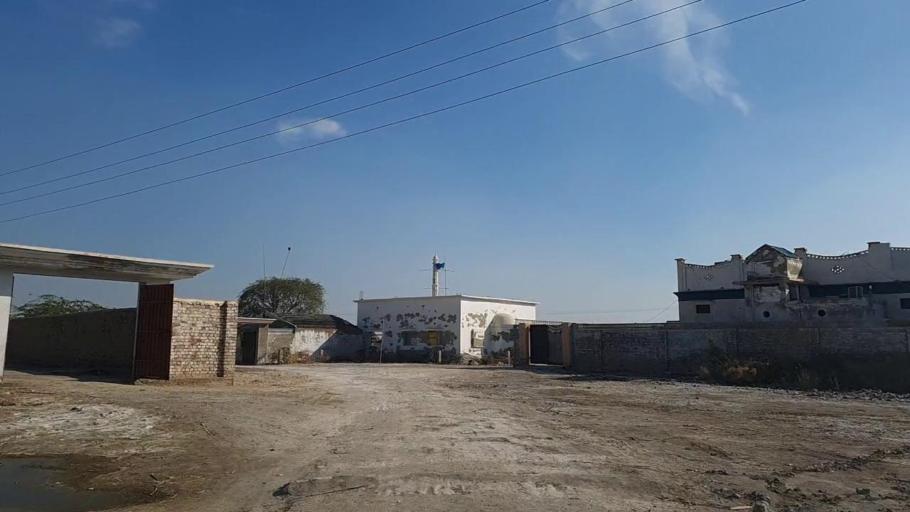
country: PK
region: Sindh
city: Bandhi
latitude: 26.5481
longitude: 68.2990
